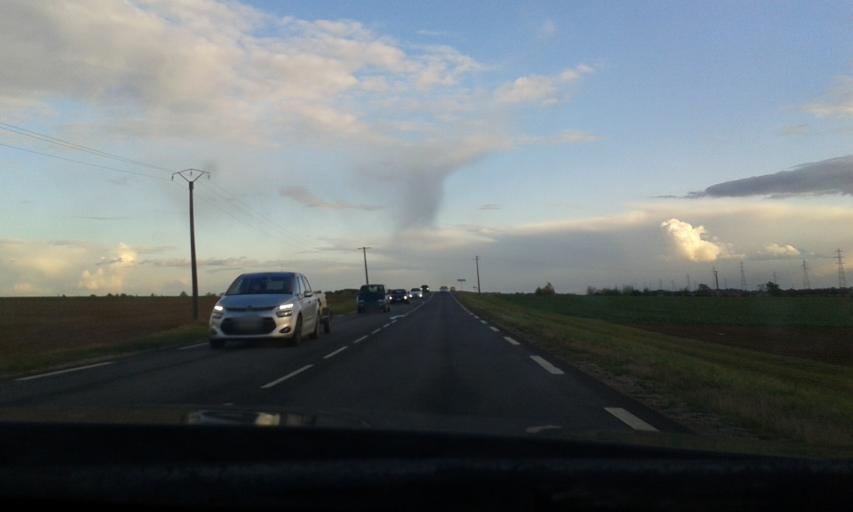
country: FR
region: Centre
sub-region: Departement d'Eure-et-Loir
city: Voves
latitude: 48.3050
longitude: 1.6923
